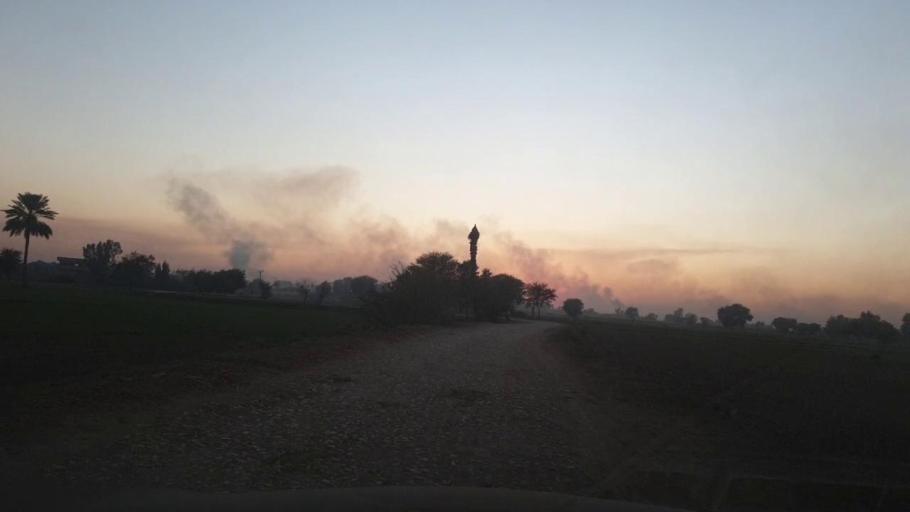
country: PK
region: Sindh
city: Ghotki
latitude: 28.0423
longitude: 69.3552
